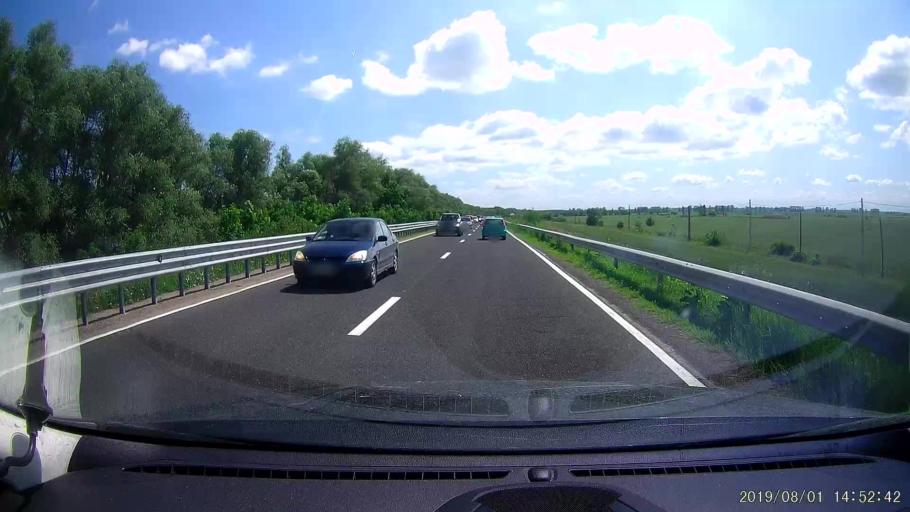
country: RO
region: Braila
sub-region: Comuna Vadeni
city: Vadeni
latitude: 45.3500
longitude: 28.0091
